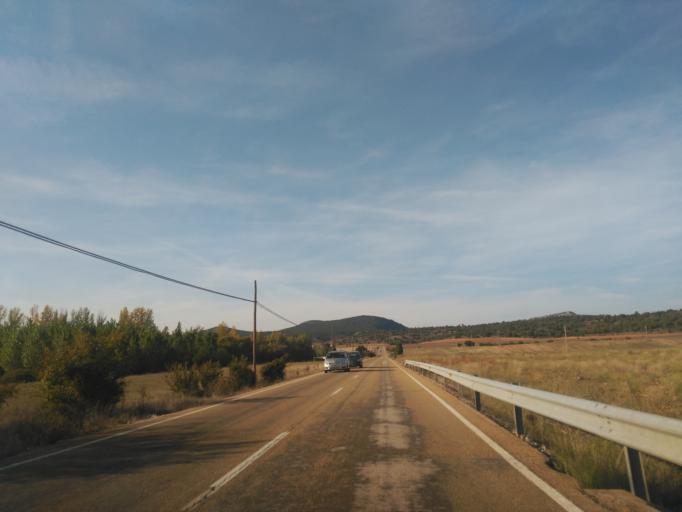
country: ES
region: Castille and Leon
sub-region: Provincia de Soria
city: Ucero
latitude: 41.7024
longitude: -3.0448
